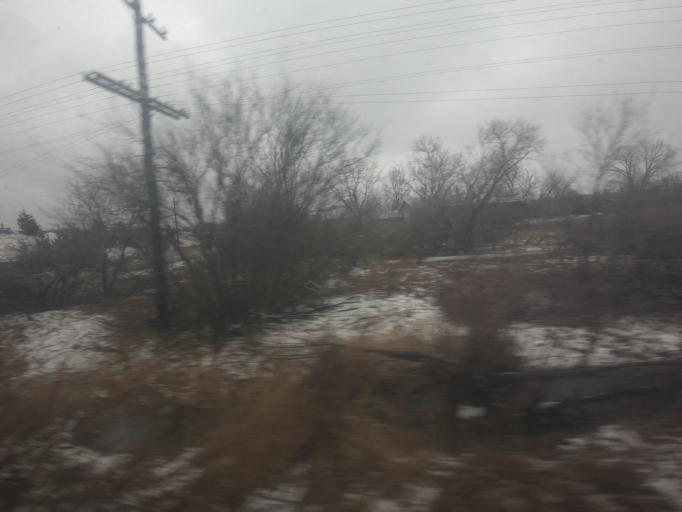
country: CA
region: Ontario
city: Deseronto
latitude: 44.2267
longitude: -77.1087
